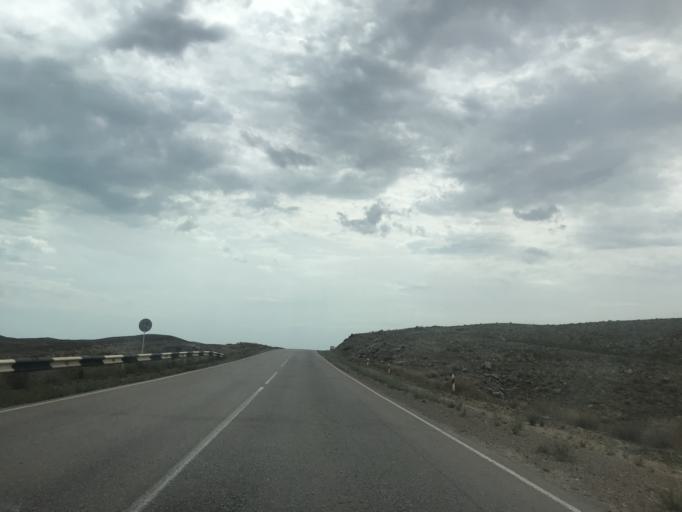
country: KZ
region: Zhambyl
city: Mynaral
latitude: 45.5061
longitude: 73.5052
